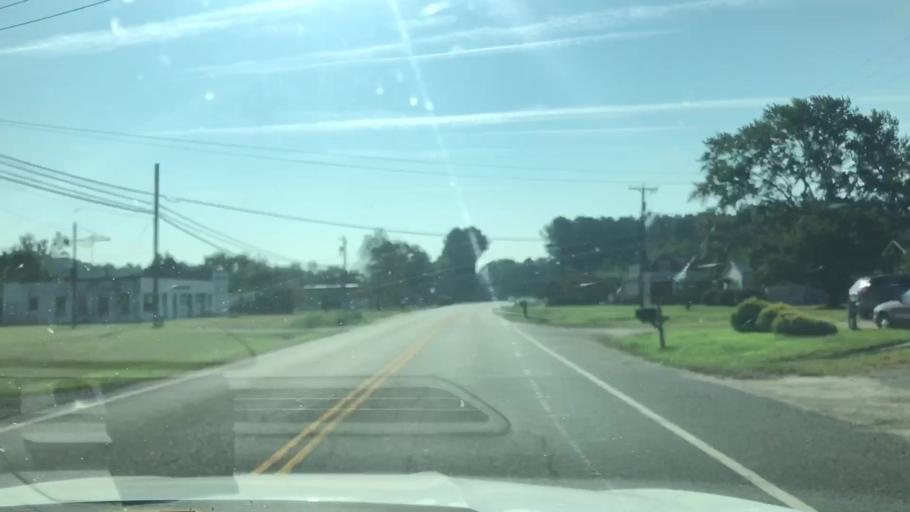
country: US
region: Virginia
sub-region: Richmond County
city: Warsaw
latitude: 37.8890
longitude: -76.6327
